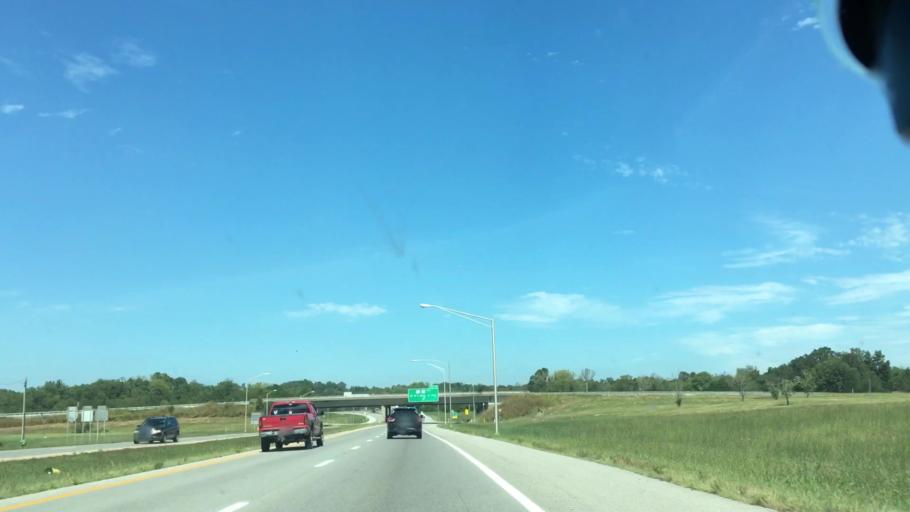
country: US
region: Kentucky
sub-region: Christian County
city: Hopkinsville
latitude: 36.8921
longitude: -87.4686
